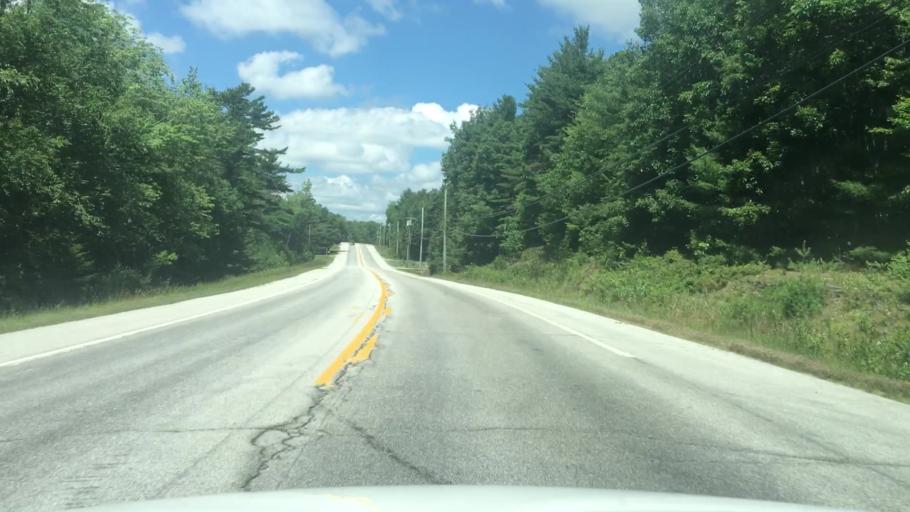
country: US
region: Maine
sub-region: Waldo County
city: Northport
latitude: 44.3565
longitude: -68.9690
